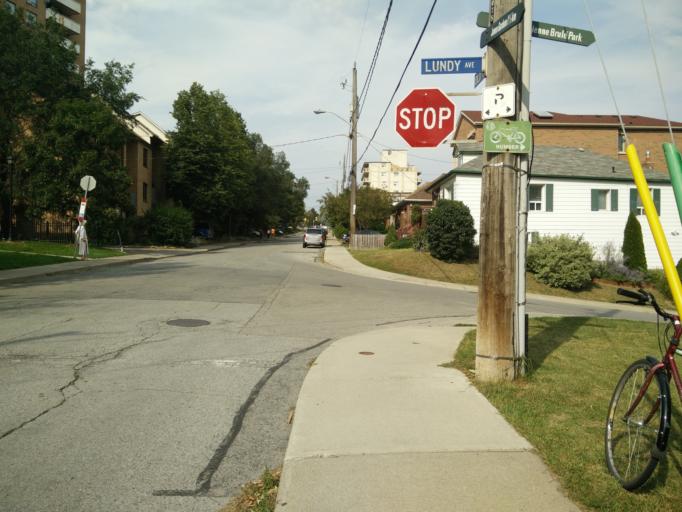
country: CA
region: Ontario
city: Etobicoke
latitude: 43.6628
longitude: -79.5036
